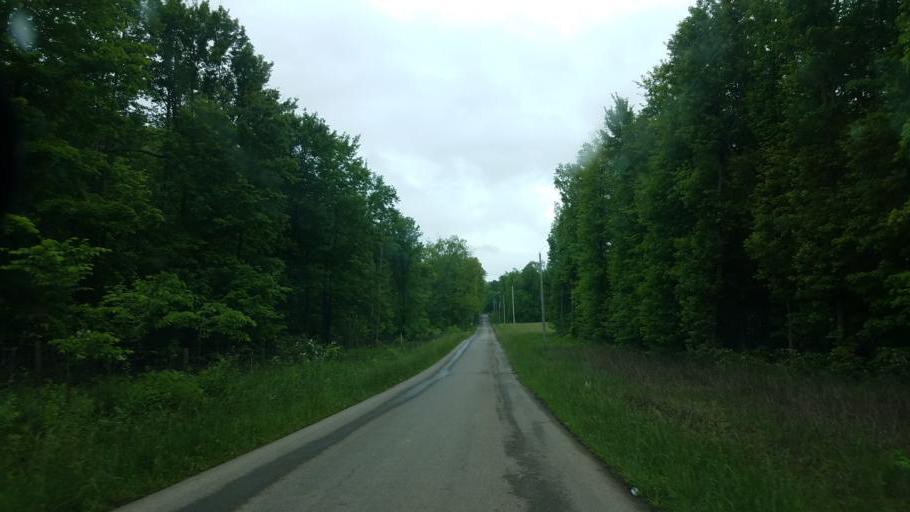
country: US
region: Ohio
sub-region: Knox County
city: Oak Hill
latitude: 40.3329
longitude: -82.2586
